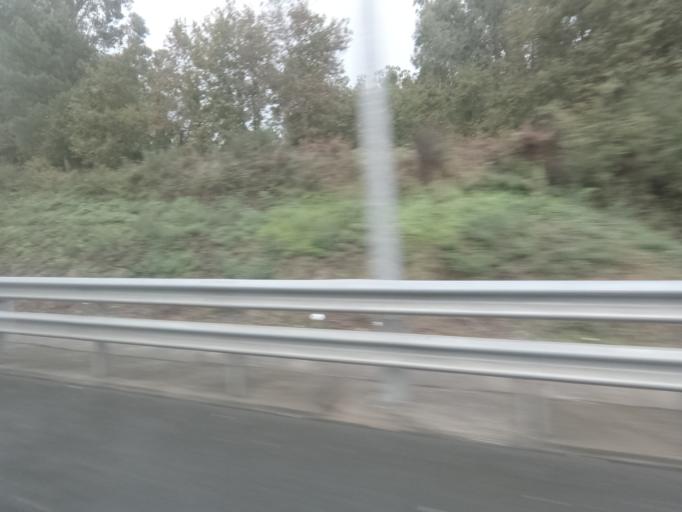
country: ES
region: Galicia
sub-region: Provincia de Pontevedra
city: Vigo
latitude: 42.2343
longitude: -8.6798
